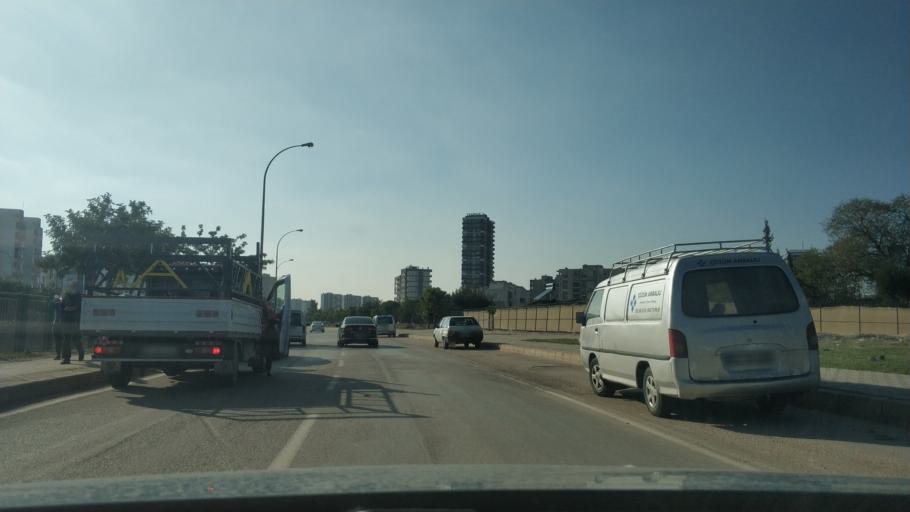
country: TR
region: Adana
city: Seyhan
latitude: 37.0118
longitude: 35.2763
